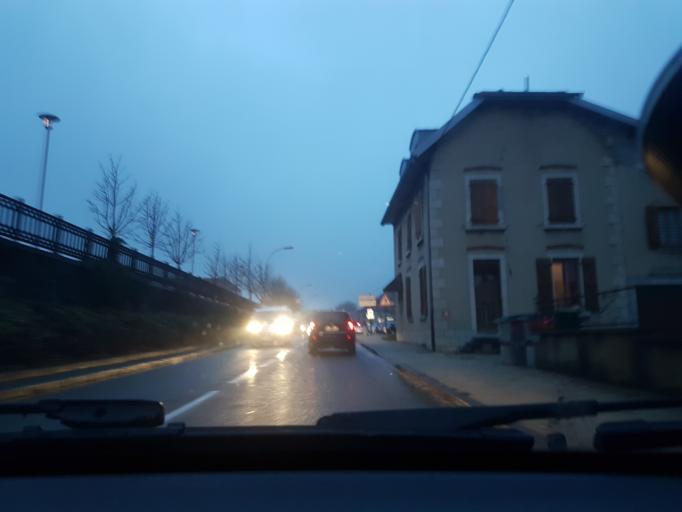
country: FR
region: Franche-Comte
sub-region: Departement du Doubs
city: Pontarlier
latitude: 46.9008
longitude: 6.3556
